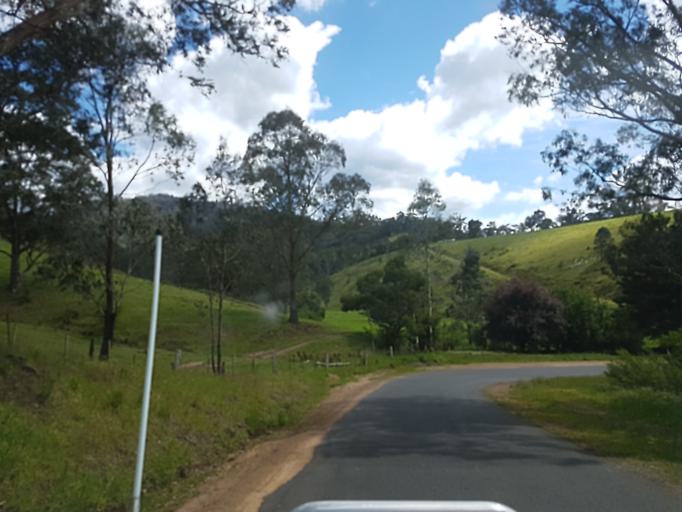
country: AU
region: Victoria
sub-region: East Gippsland
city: Bairnsdale
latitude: -37.4321
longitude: 147.2491
